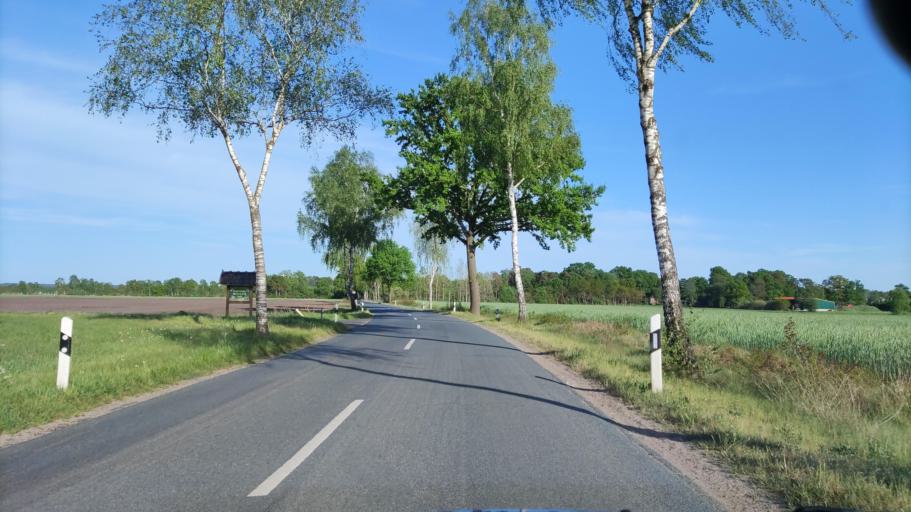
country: DE
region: Lower Saxony
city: Schneverdingen
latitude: 53.1755
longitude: 9.8002
